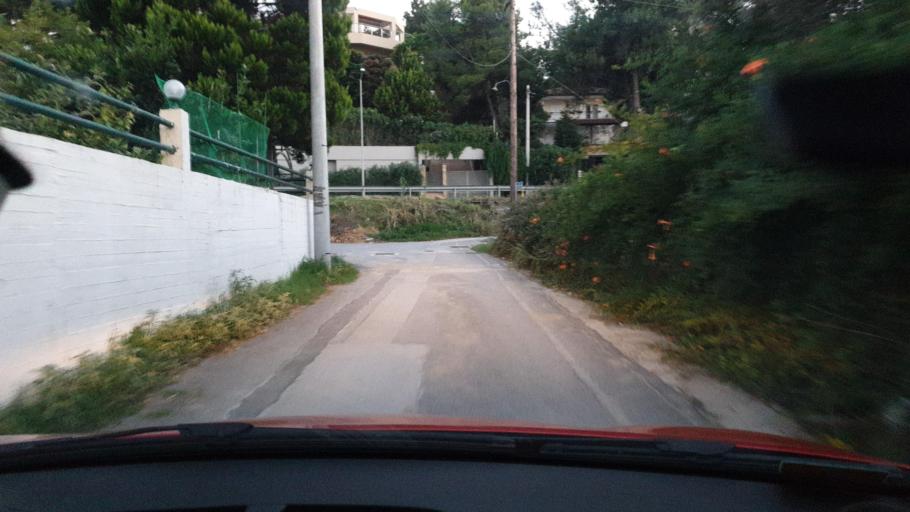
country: GR
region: Central Macedonia
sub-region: Nomos Thessalonikis
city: Neoi Epivates
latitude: 40.5005
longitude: 22.8931
